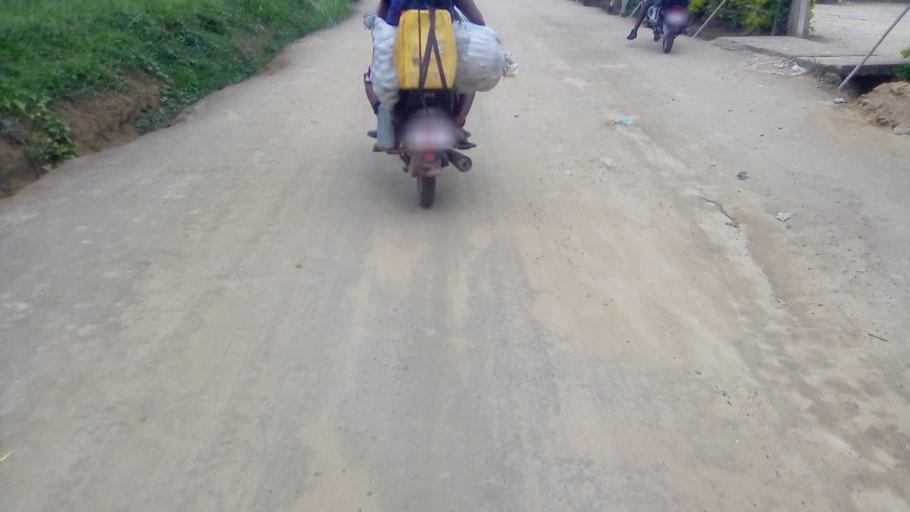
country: SL
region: Southern Province
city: Bo
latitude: 7.9403
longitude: -11.7426
